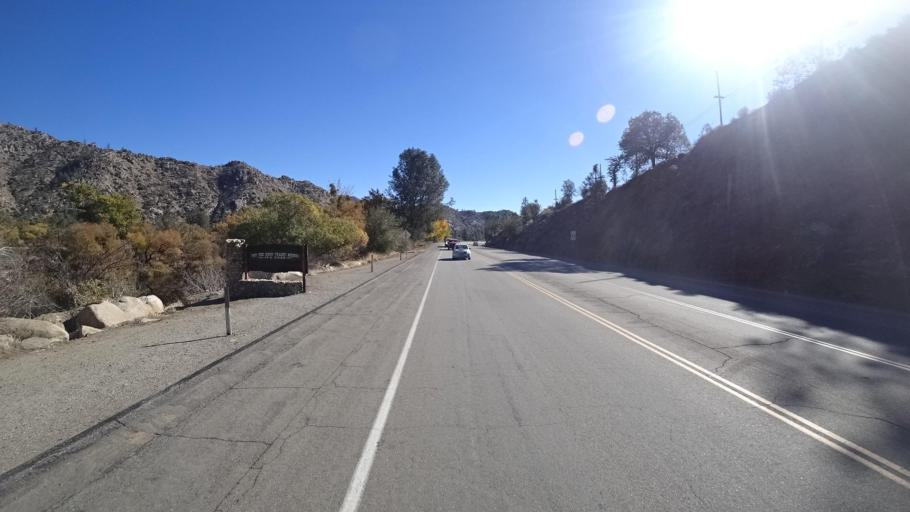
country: US
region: California
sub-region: Kern County
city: Kernville
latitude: 35.7511
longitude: -118.4224
